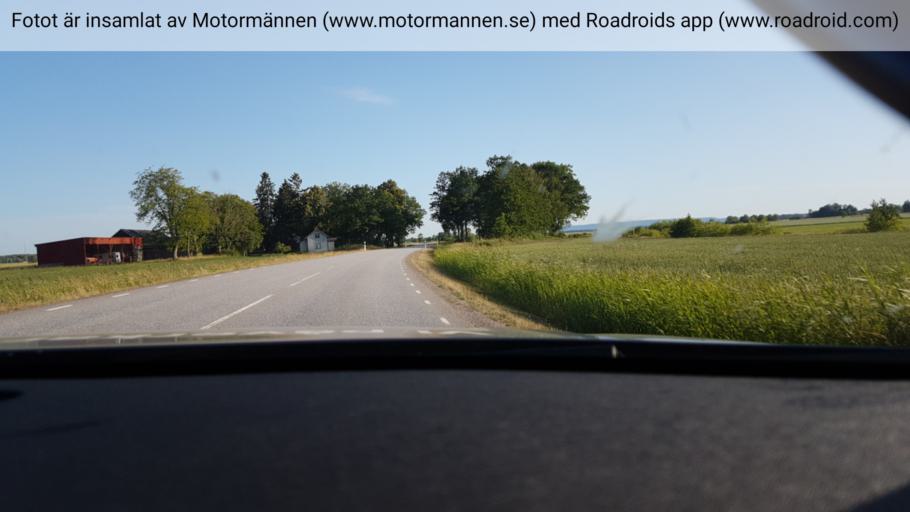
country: SE
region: Vaestra Goetaland
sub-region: Toreboda Kommun
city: Toereboda
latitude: 58.6195
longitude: 14.0133
